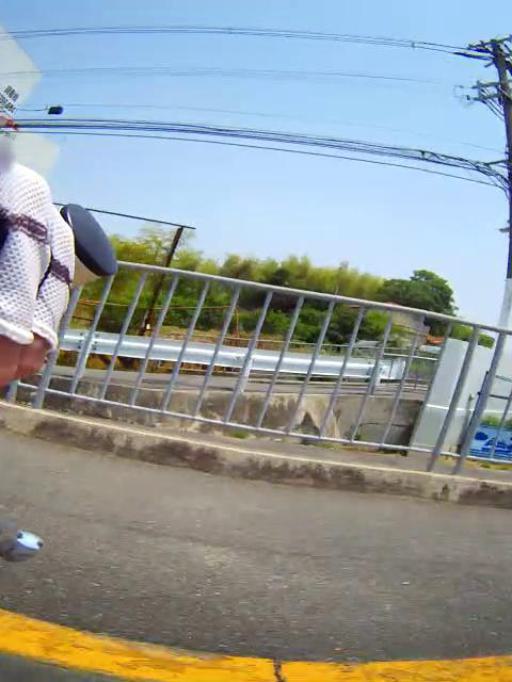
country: JP
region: Osaka
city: Suita
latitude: 34.7817
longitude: 135.4973
